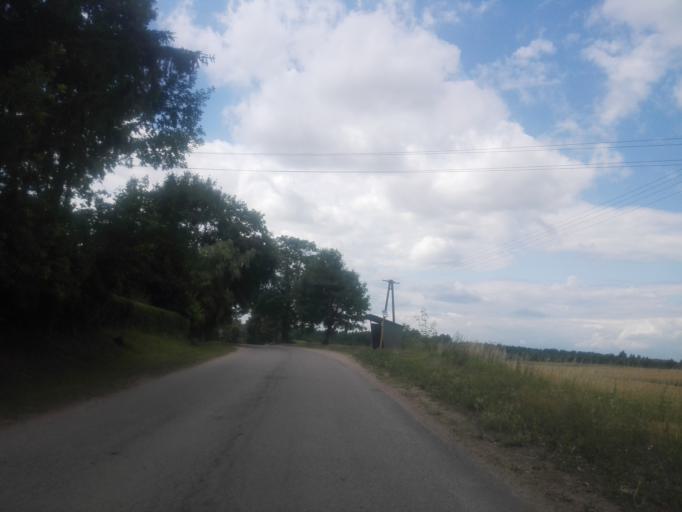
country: PL
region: Podlasie
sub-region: Powiat sejnenski
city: Sejny
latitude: 54.1374
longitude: 23.4182
